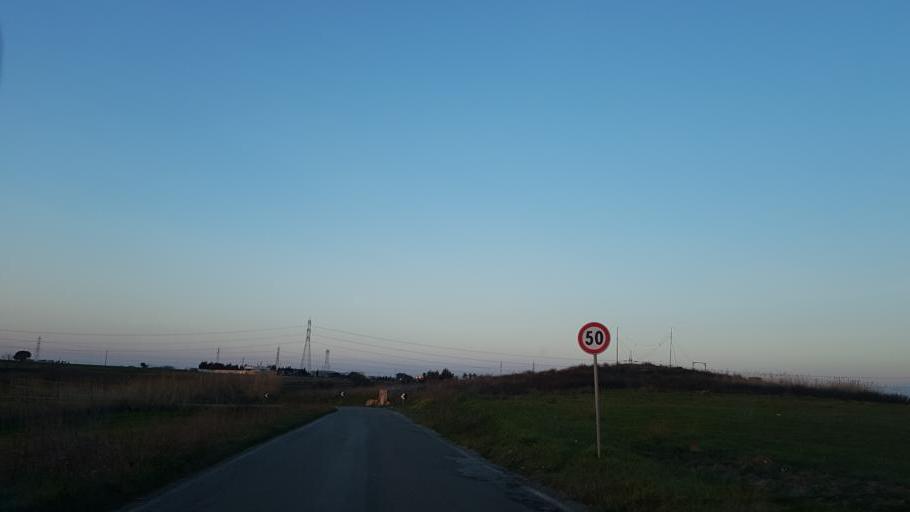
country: IT
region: Apulia
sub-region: Provincia di Brindisi
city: La Rosa
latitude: 40.5909
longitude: 17.9198
